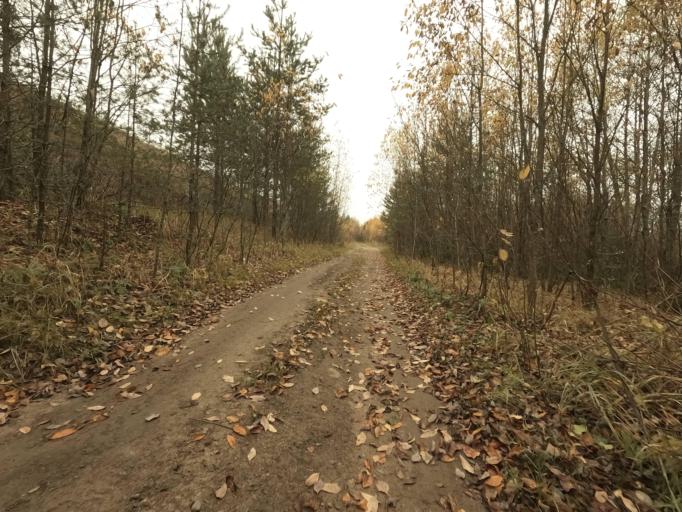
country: RU
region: Leningrad
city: Pavlovo
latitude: 59.7756
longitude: 30.9015
